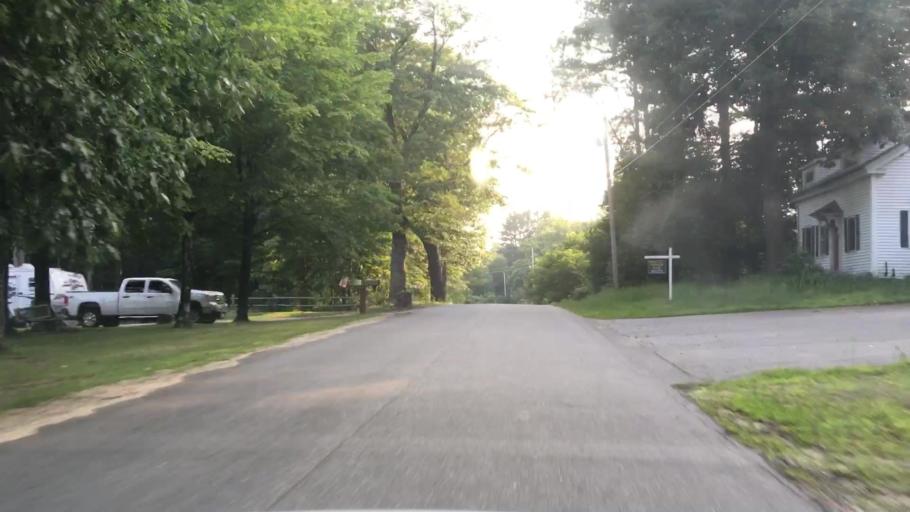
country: US
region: Maine
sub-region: Oxford County
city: Bethel
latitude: 44.4105
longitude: -70.8663
